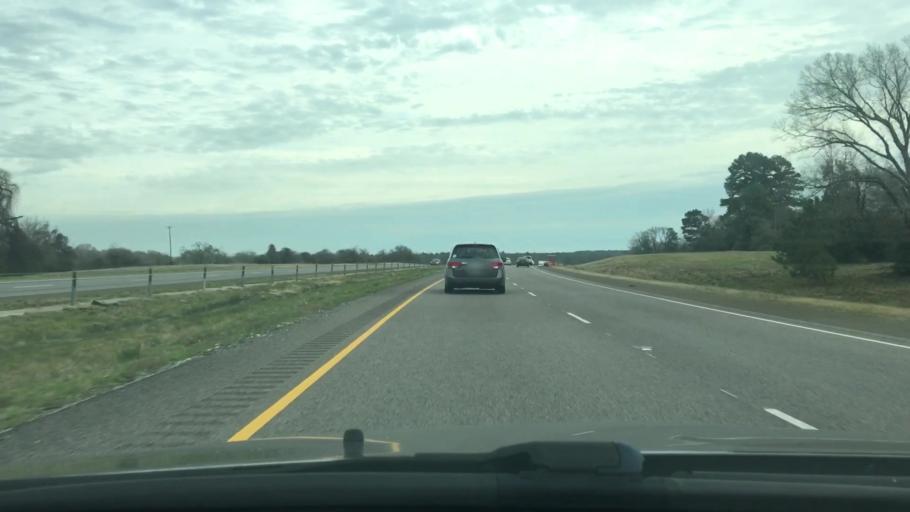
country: US
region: Texas
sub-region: Madison County
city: Madisonville
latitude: 30.9098
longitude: -95.7908
